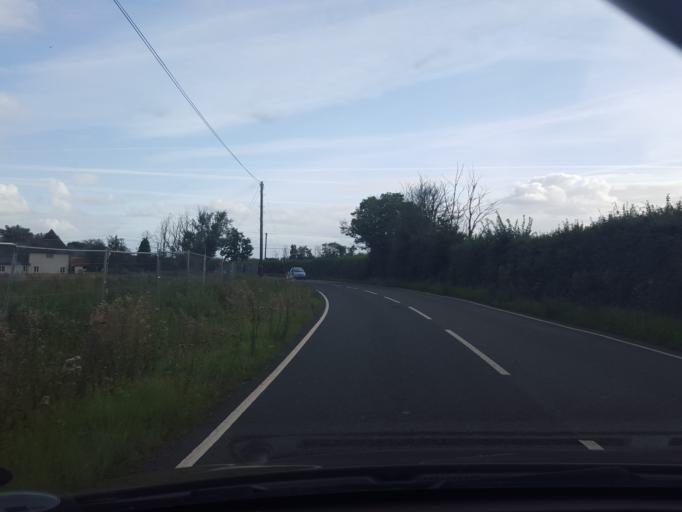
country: GB
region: England
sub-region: Essex
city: Little Clacton
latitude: 51.8234
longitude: 1.1613
